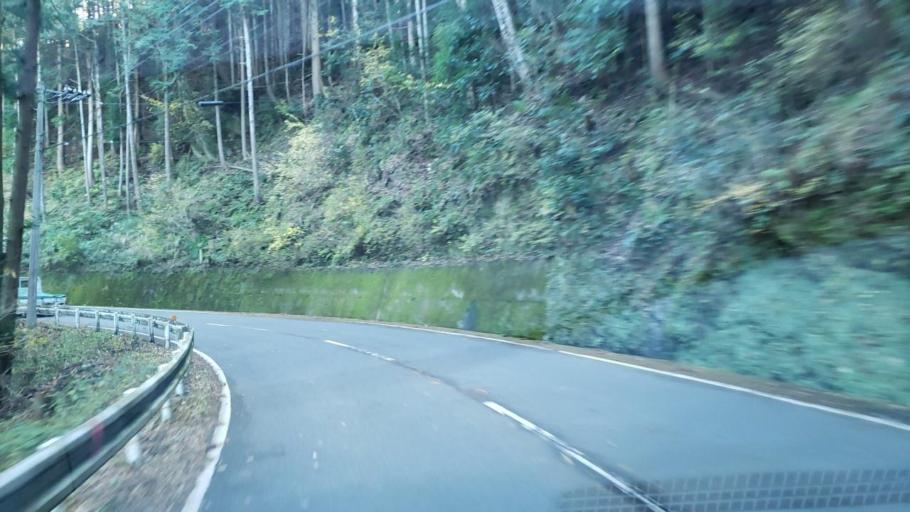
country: JP
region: Tokushima
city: Wakimachi
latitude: 34.0026
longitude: 134.0358
